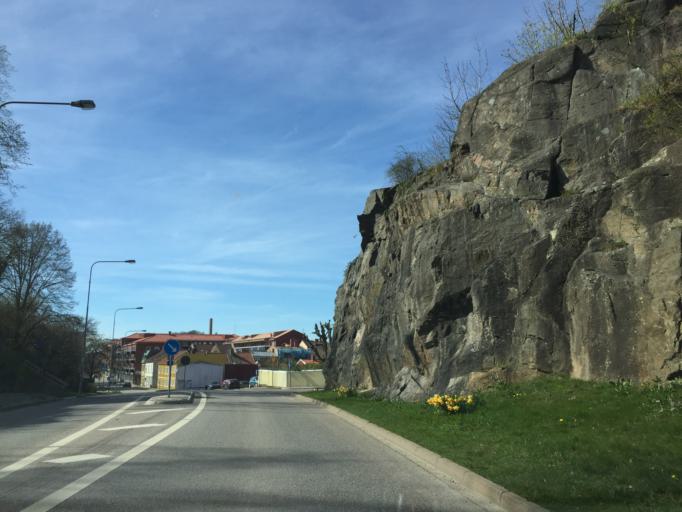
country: SE
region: Vaestra Goetaland
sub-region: Uddevalla Kommun
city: Uddevalla
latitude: 58.3469
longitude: 11.9380
